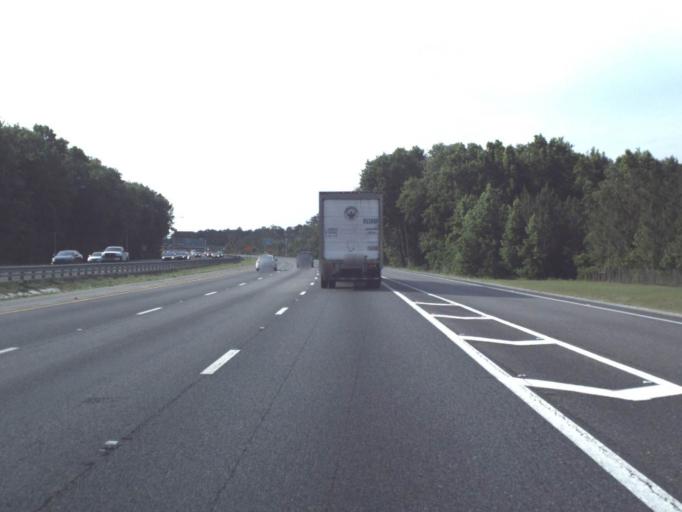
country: US
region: Florida
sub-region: Saint Johns County
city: Palm Valley
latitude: 30.0962
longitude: -81.4985
